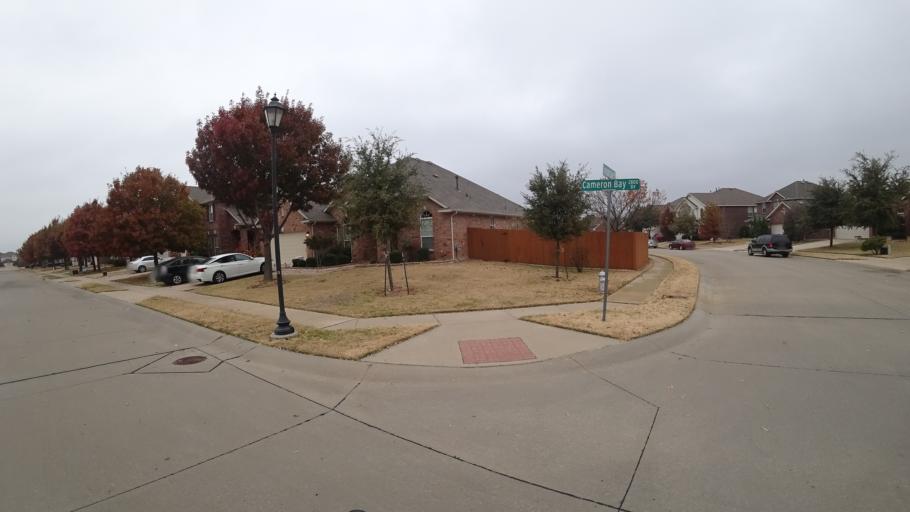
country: US
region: Texas
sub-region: Denton County
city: The Colony
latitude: 33.0680
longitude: -96.9040
